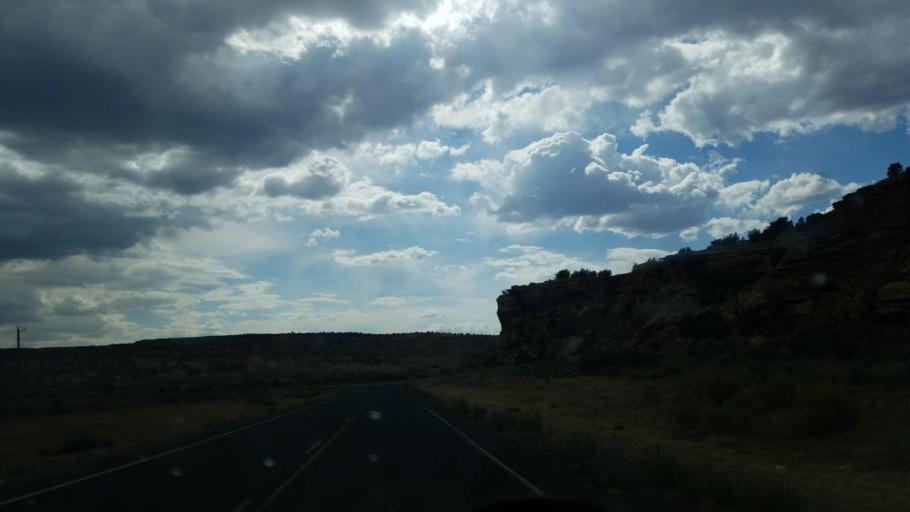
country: US
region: Arizona
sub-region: Apache County
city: Saint Michaels
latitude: 35.4154
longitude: -108.9867
